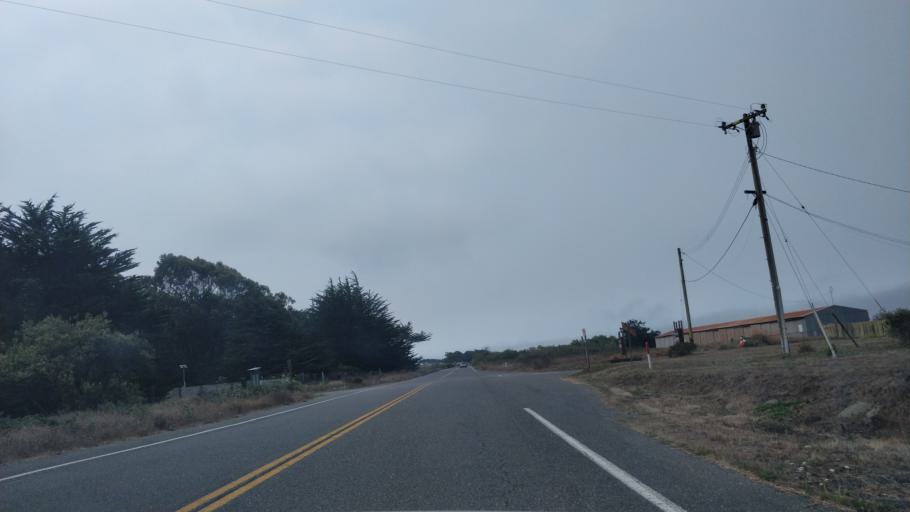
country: US
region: California
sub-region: Humboldt County
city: Bayview
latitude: 40.7797
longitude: -124.2077
